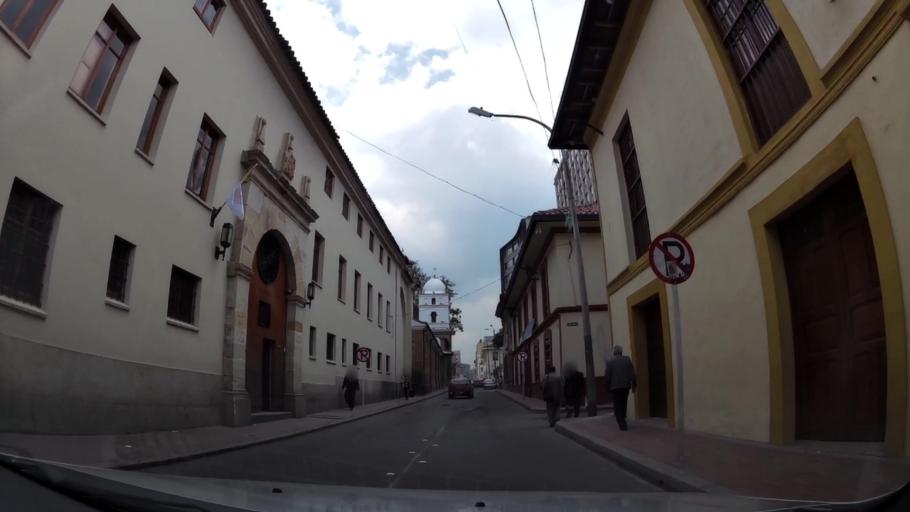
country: CO
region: Bogota D.C.
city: Bogota
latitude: 4.5935
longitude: -74.0781
